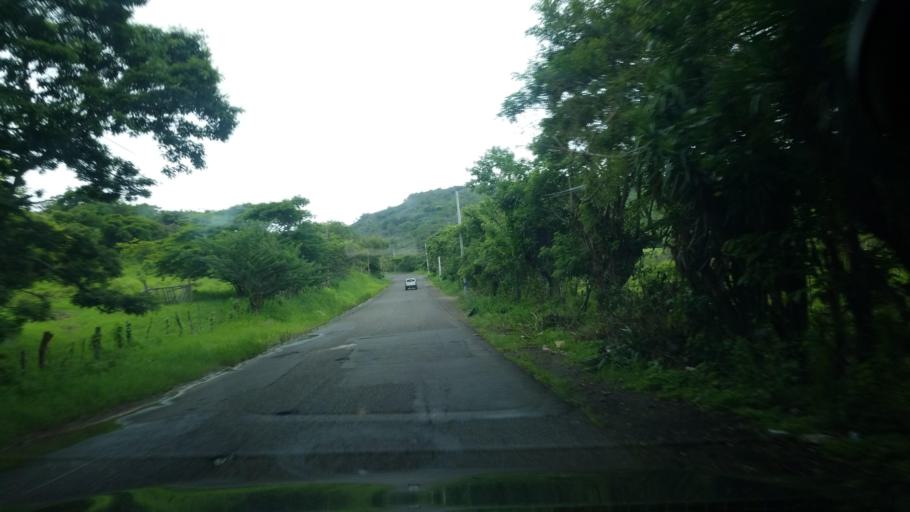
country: HN
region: Choluteca
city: San Marcos de Colon
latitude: 13.4253
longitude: -86.8319
